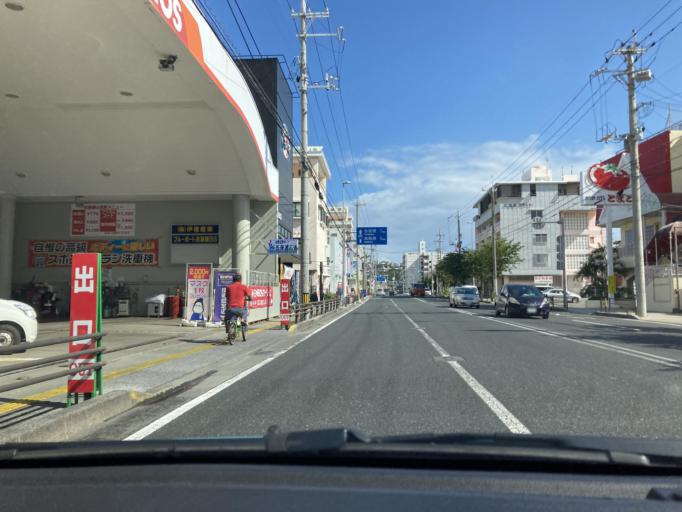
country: JP
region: Okinawa
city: Tomigusuku
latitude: 26.1988
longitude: 127.6882
